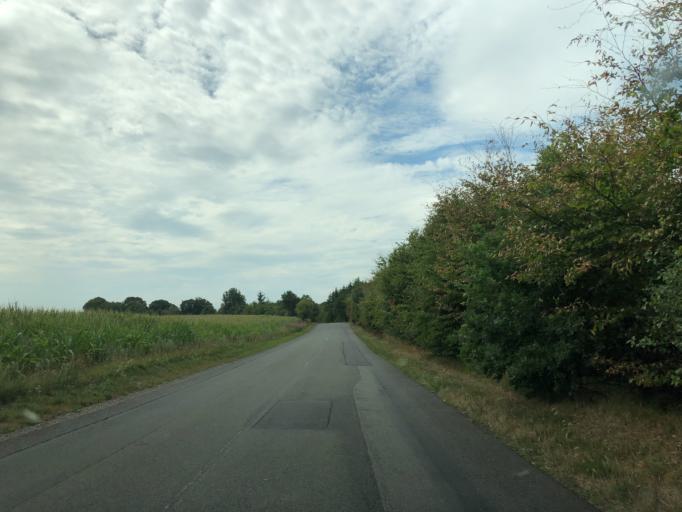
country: DK
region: South Denmark
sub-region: Vejle Kommune
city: Egtved
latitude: 55.6395
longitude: 9.1997
